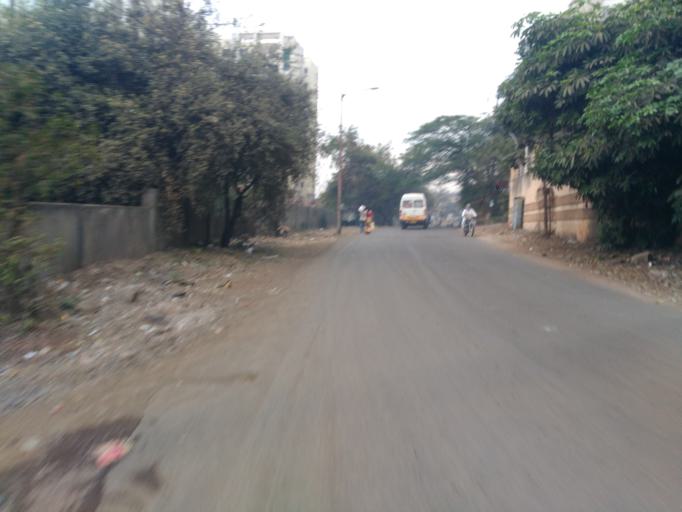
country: IN
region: Maharashtra
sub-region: Pune Division
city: Pune
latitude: 18.4613
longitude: 73.8885
